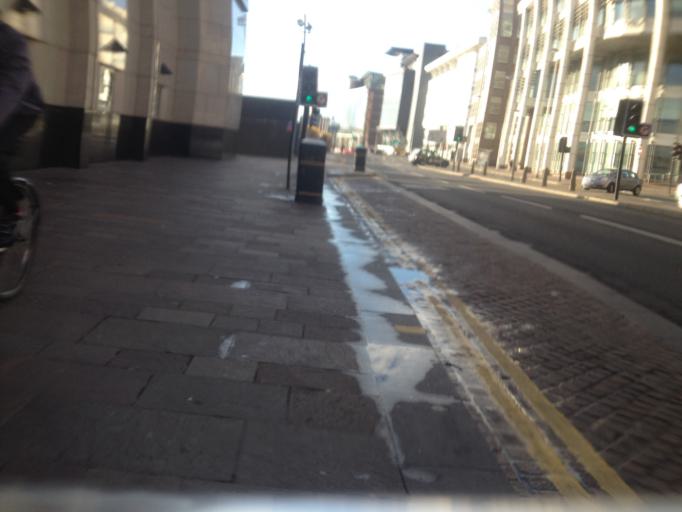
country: GB
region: Scotland
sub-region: Glasgow City
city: Glasgow
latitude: 55.8566
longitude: -4.2602
